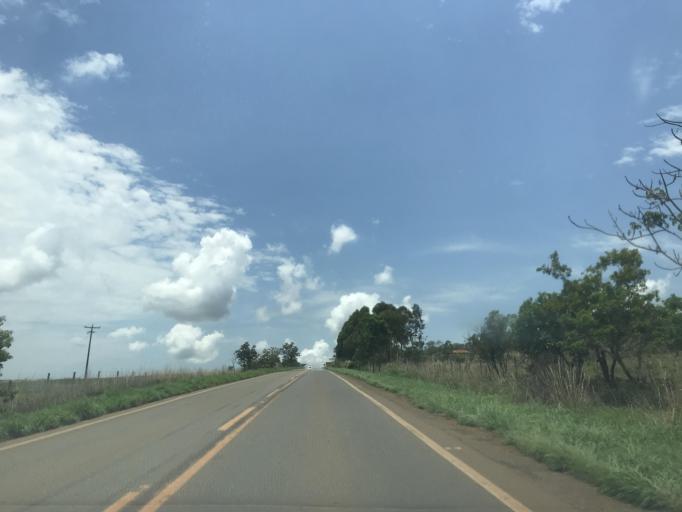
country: BR
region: Goias
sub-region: Luziania
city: Luziania
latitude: -16.4862
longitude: -48.2025
